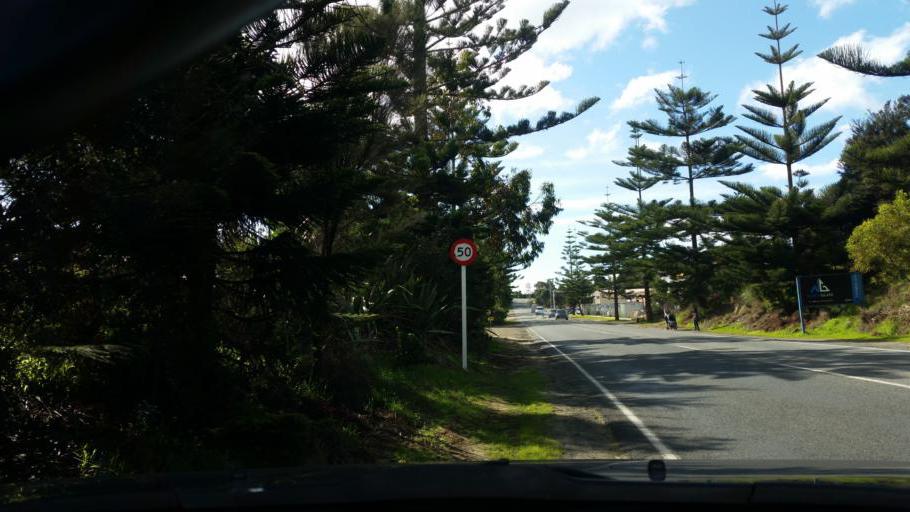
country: NZ
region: Auckland
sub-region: Auckland
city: Wellsford
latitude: -36.1035
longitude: 174.5855
